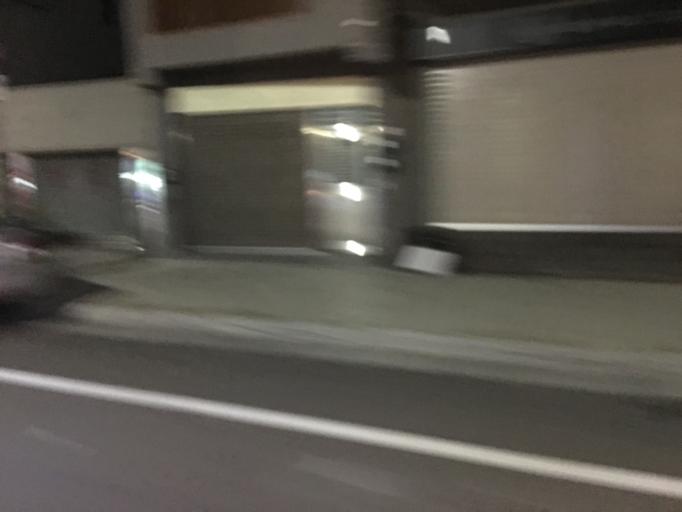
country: TW
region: Taiwan
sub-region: Hsinchu
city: Hsinchu
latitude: 24.7996
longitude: 120.9499
